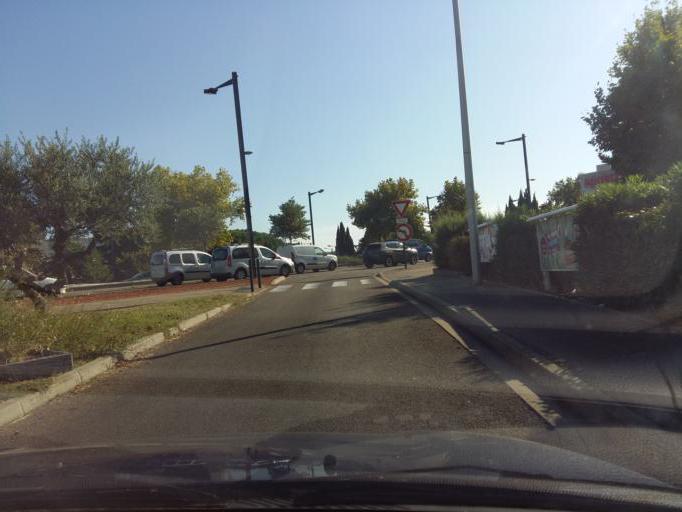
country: FR
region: Languedoc-Roussillon
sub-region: Departement du Gard
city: Nimes
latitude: 43.8172
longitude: 4.3450
